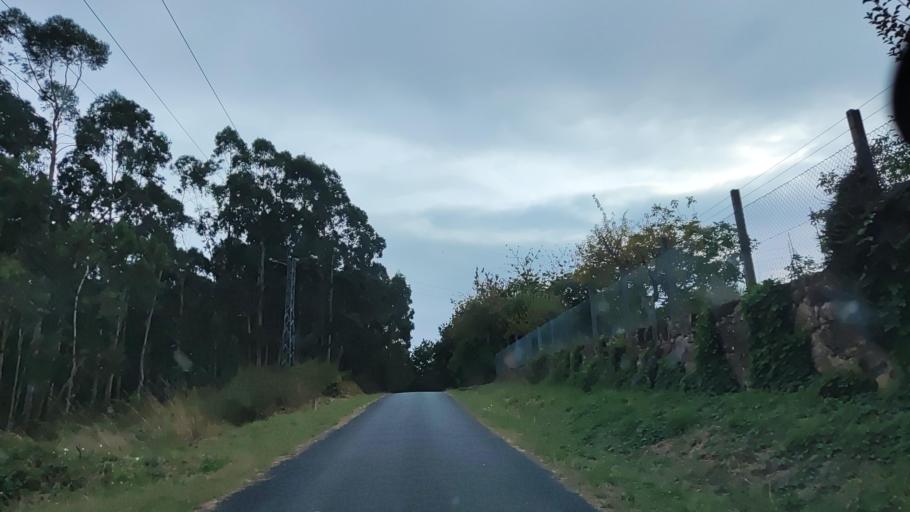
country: ES
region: Galicia
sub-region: Provincia da Coruna
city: Padron
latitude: 42.7205
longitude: -8.6796
